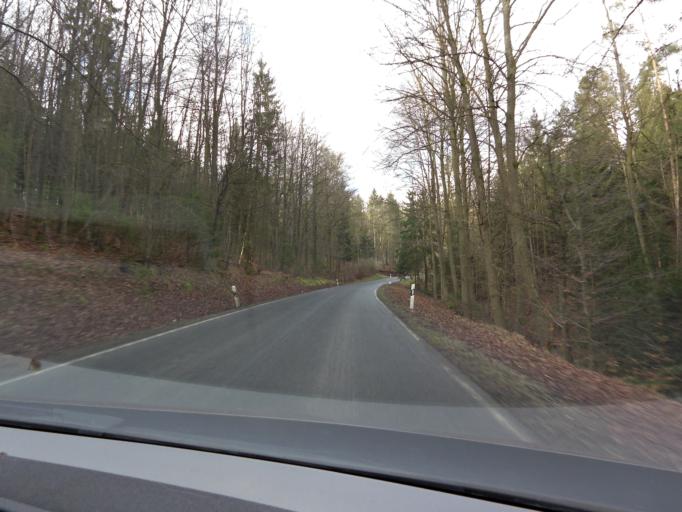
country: DE
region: Thuringia
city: Creuzburg
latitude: 51.0704
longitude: 10.2265
